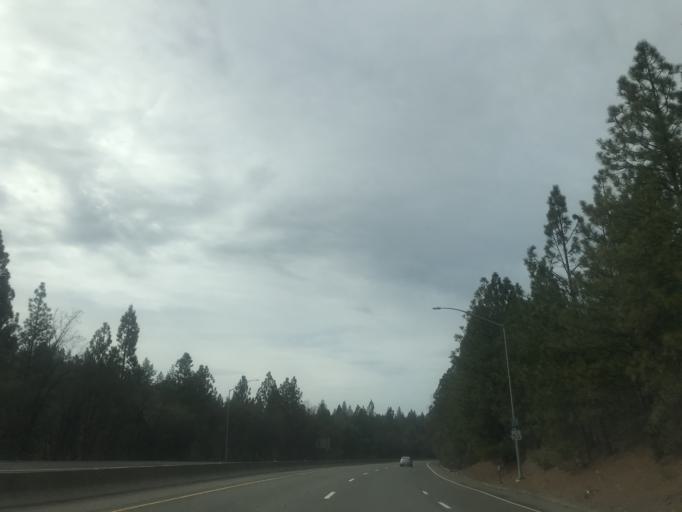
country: US
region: California
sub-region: El Dorado County
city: Placerville
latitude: 38.7306
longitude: -120.7624
